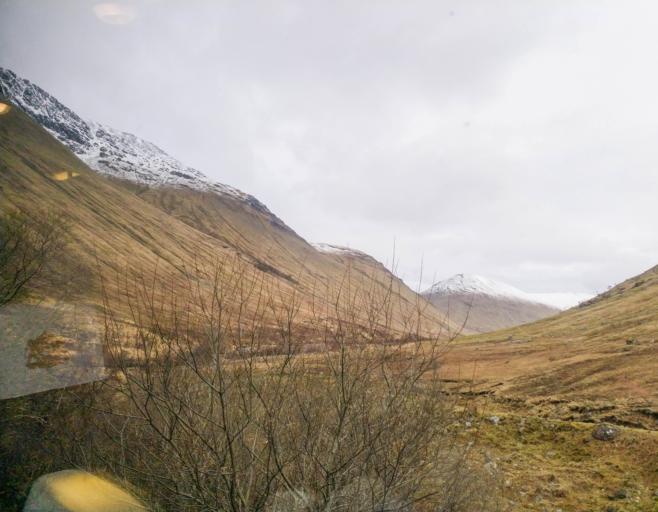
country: GB
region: Scotland
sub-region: Argyll and Bute
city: Garelochhead
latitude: 56.4881
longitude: -4.7034
